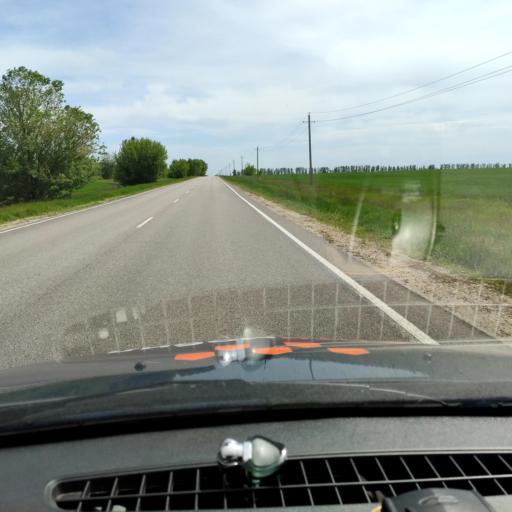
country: RU
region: Voronezj
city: Novaya Usman'
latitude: 51.5752
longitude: 39.3751
